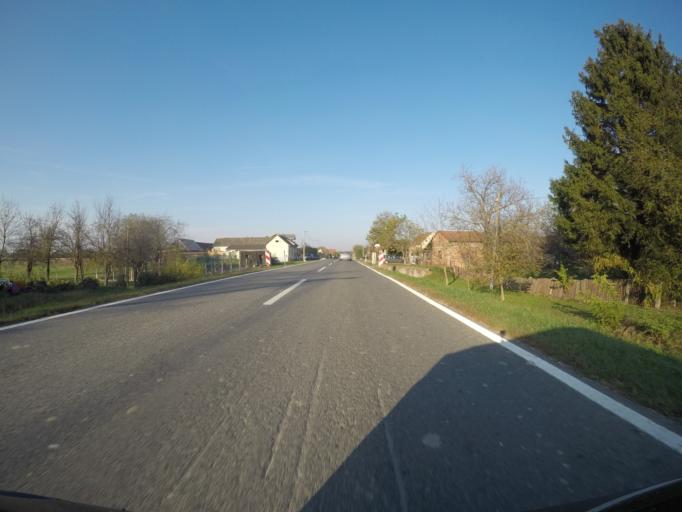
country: HU
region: Somogy
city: Barcs
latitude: 45.9304
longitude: 17.4587
